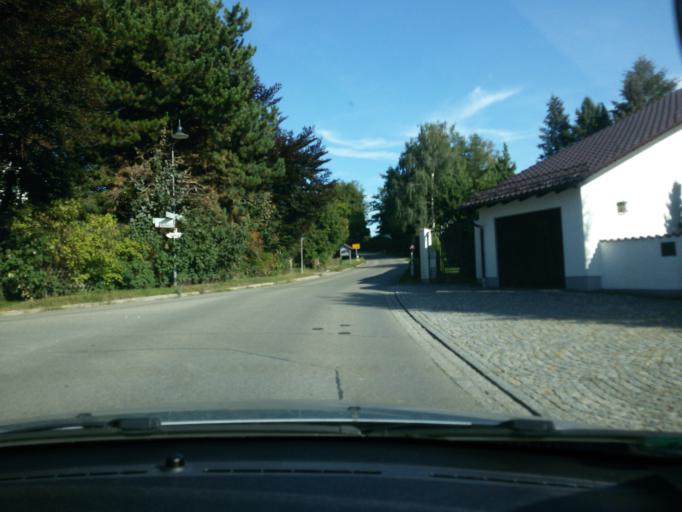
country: DE
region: Bavaria
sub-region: Swabia
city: Kutzenhausen
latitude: 48.3431
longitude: 10.6994
